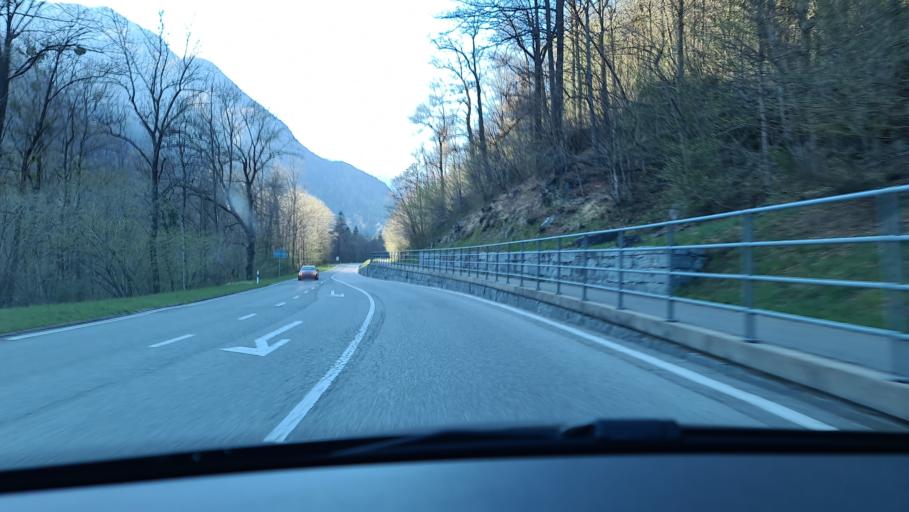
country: CH
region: Ticino
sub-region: Locarno District
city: Verscio
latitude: 46.2528
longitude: 8.6990
